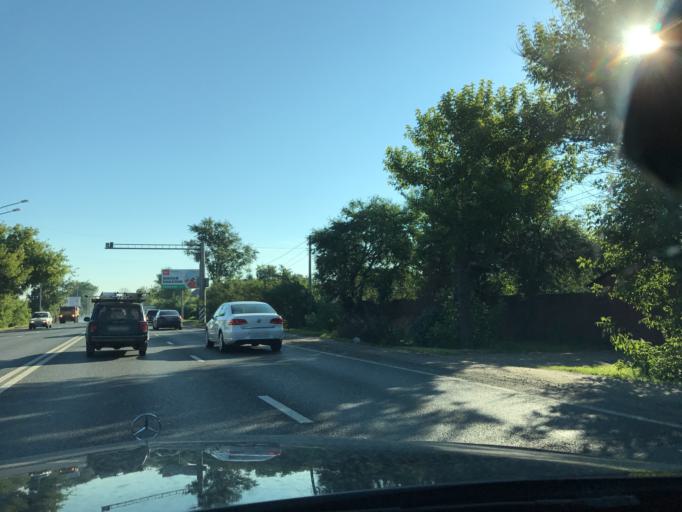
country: RU
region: Moskovskaya
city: Medvezh'i Ozera
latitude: 55.8571
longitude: 37.9799
